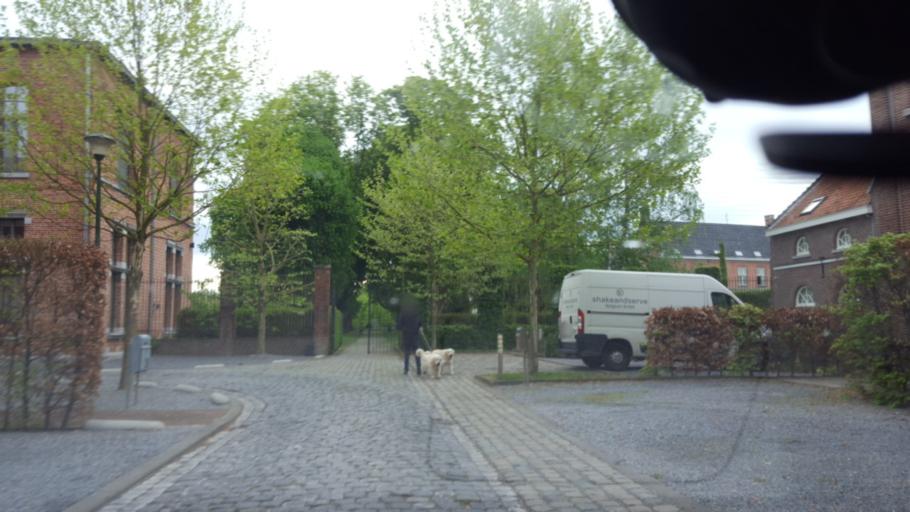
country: BE
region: Flanders
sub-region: Provincie Limburg
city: Maasmechelen
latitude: 50.9255
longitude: 5.7030
